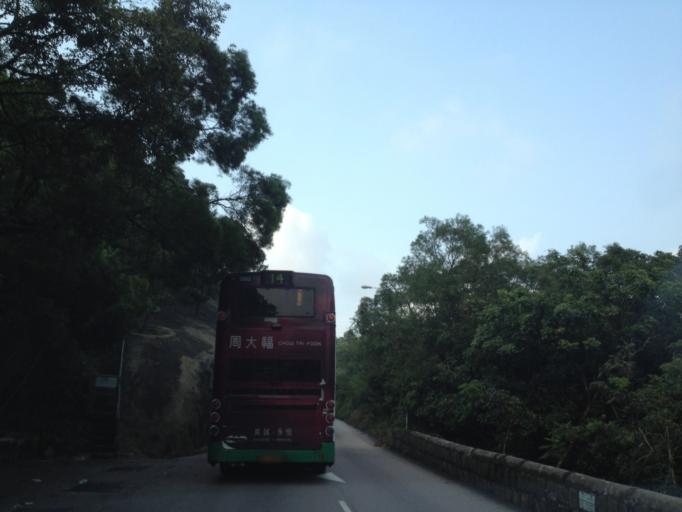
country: HK
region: Wanchai
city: Wan Chai
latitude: 22.2556
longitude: 114.2277
